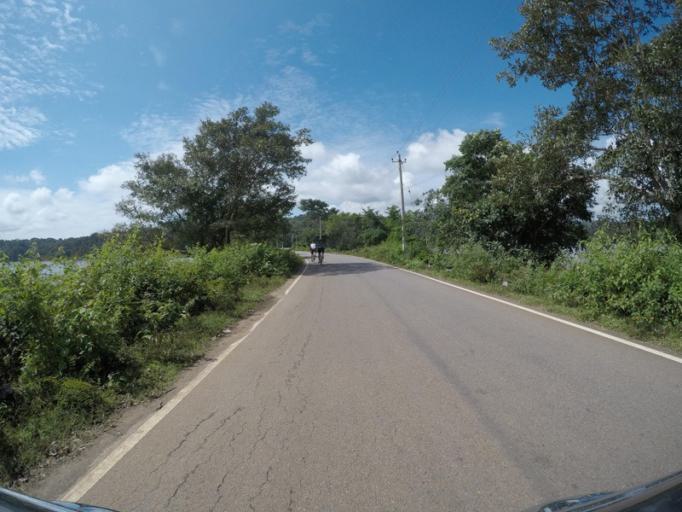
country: IN
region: Karnataka
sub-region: Kodagu
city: Suntikoppa
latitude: 12.4962
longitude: 75.8232
